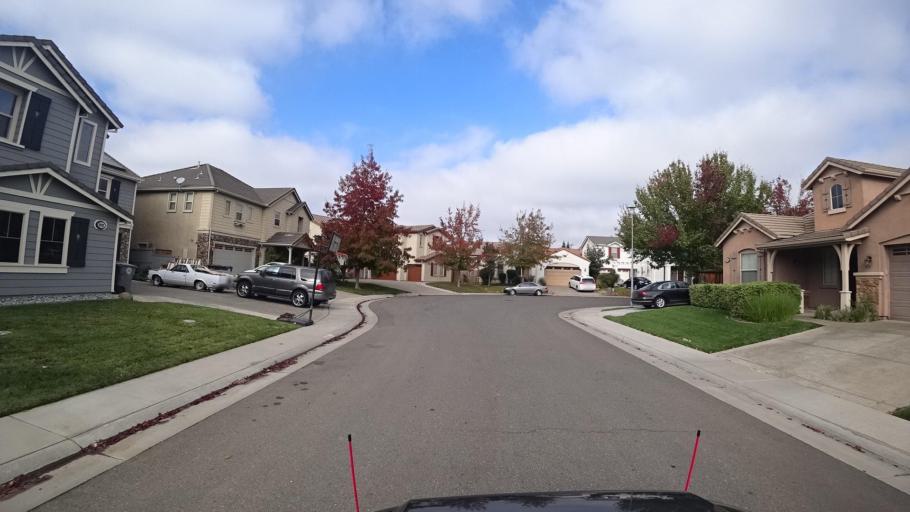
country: US
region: California
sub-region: Sacramento County
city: Elk Grove
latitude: 38.4221
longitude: -121.3665
